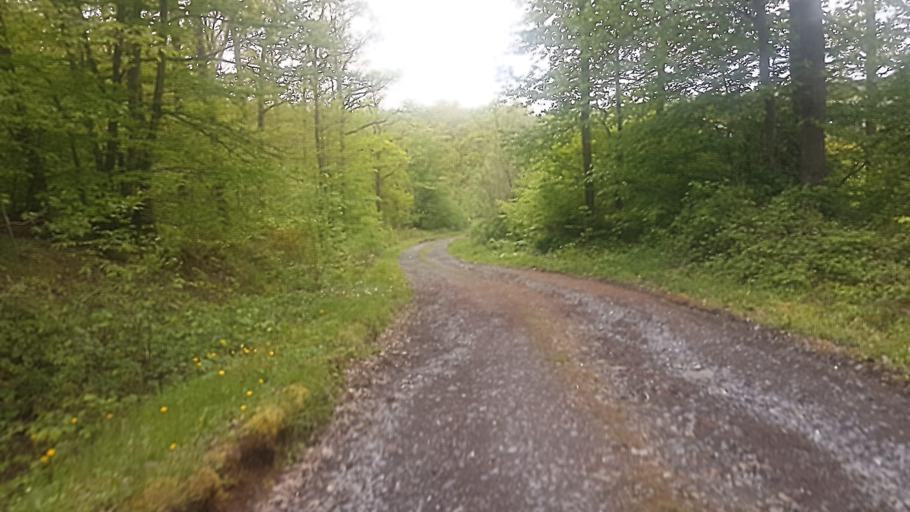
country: FR
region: Champagne-Ardenne
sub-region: Departement des Ardennes
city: Vireux-Molhain
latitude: 50.0677
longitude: 4.6181
